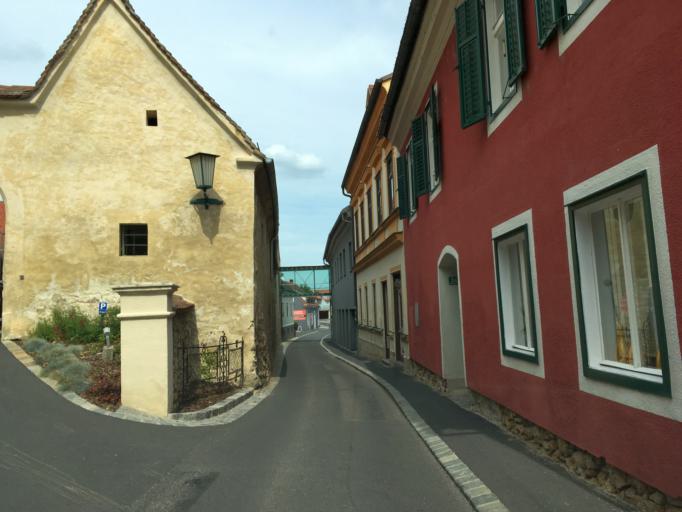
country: AT
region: Styria
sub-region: Politischer Bezirk Hartberg-Fuerstenfeld
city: Hartberg
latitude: 47.2806
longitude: 15.9702
